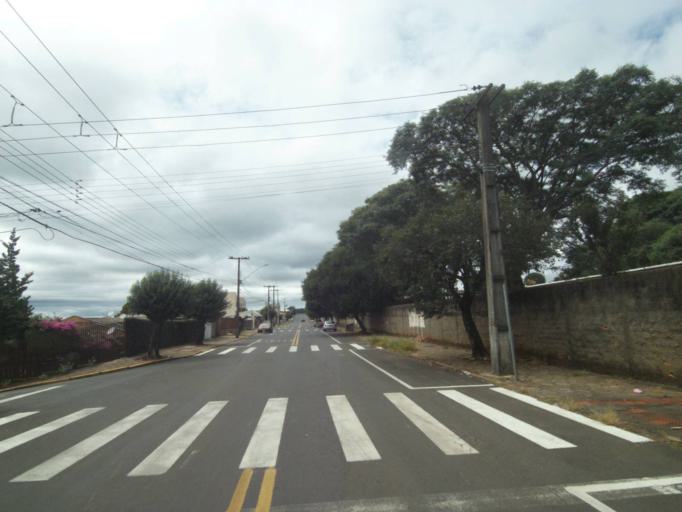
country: BR
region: Parana
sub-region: Telemaco Borba
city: Telemaco Borba
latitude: -24.3386
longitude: -50.6216
